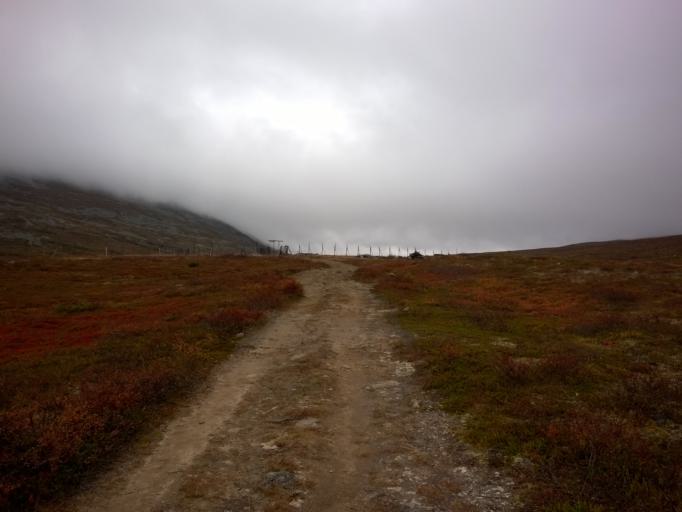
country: FI
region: Lapland
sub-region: Tunturi-Lappi
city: Muonio
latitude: 68.0546
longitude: 24.0754
